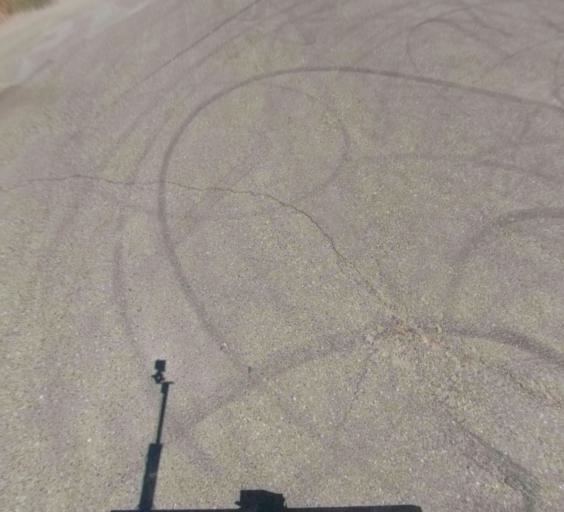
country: US
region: California
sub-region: Madera County
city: Parksdale
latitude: 36.9214
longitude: -119.9791
